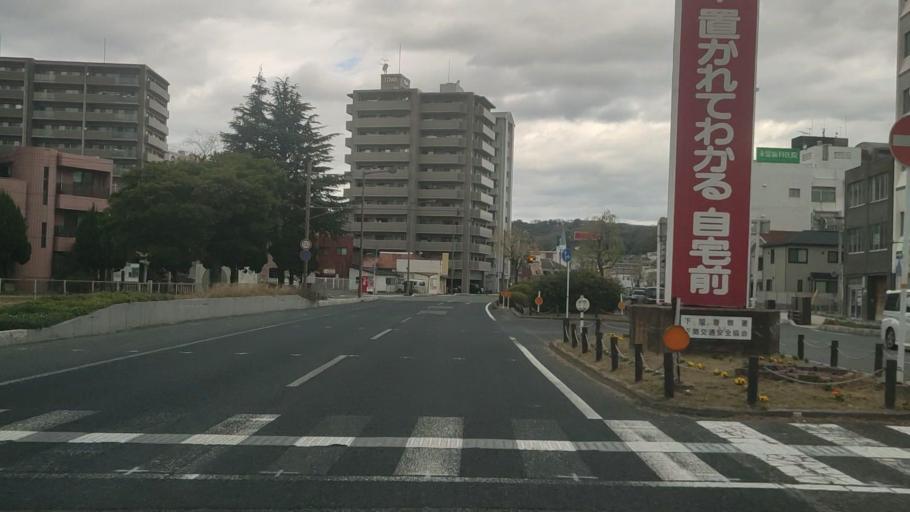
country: JP
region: Yamaguchi
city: Shimonoseki
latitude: 33.9606
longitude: 130.9417
